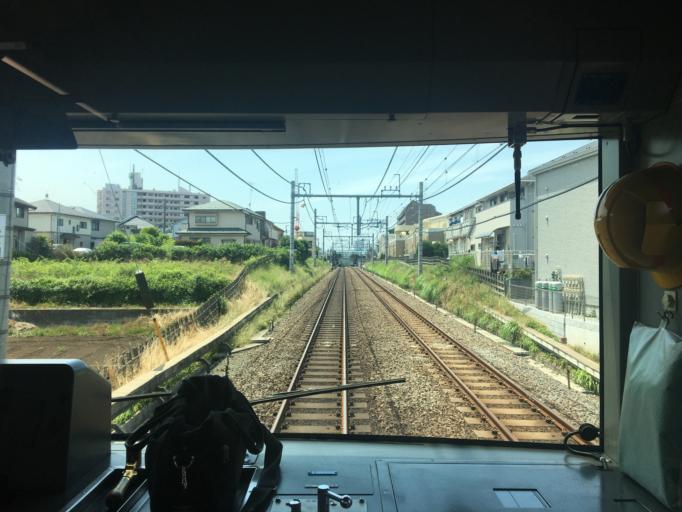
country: JP
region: Saitama
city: Tokorozawa
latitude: 35.7774
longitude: 139.5007
